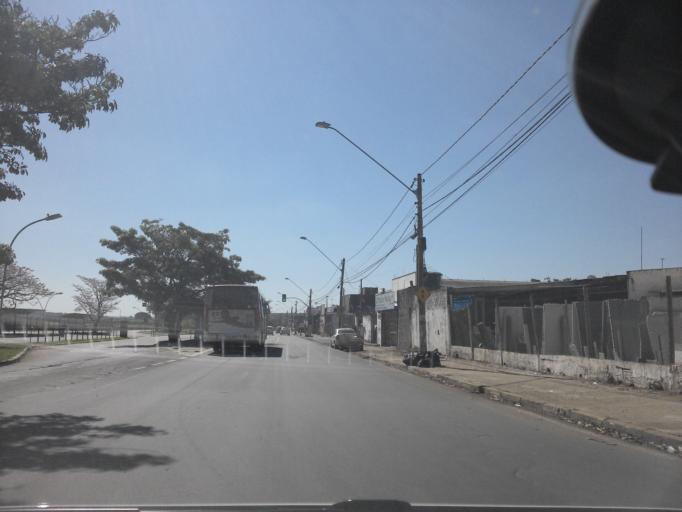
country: BR
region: Sao Paulo
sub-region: Campinas
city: Campinas
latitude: -22.8573
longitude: -47.1087
